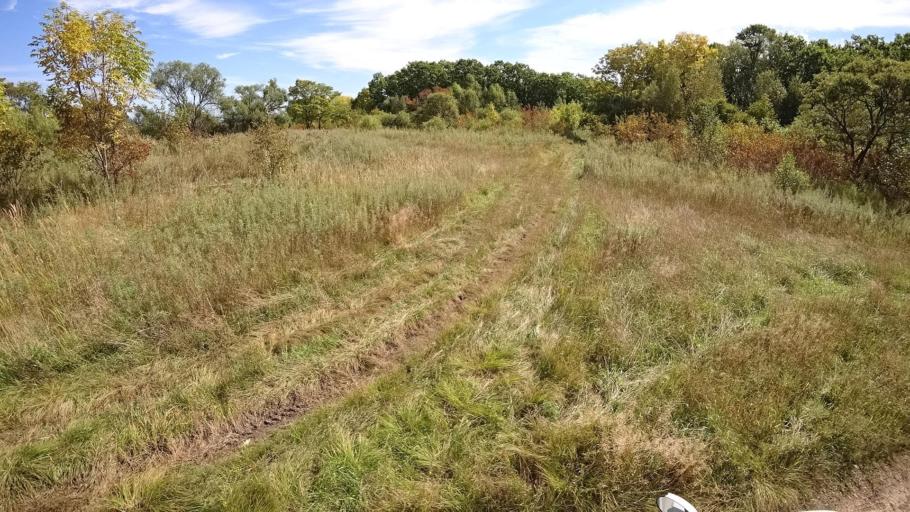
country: RU
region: Primorskiy
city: Kirovskiy
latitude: 44.7583
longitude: 133.6194
